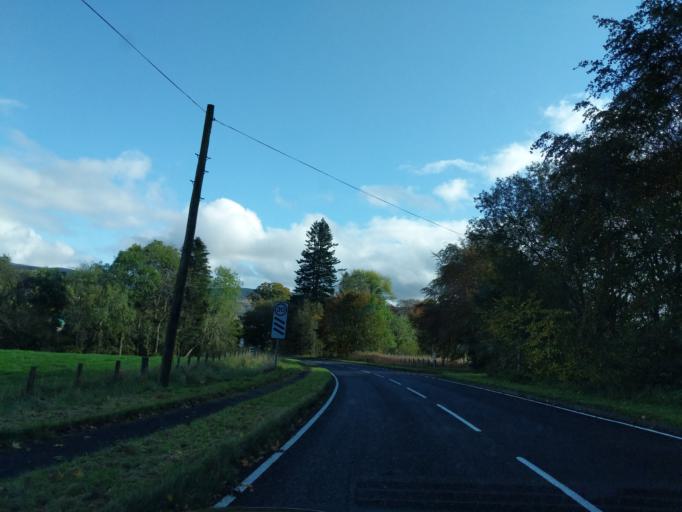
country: GB
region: Scotland
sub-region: Dumfries and Galloway
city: Moffat
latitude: 55.3378
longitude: -3.4555
